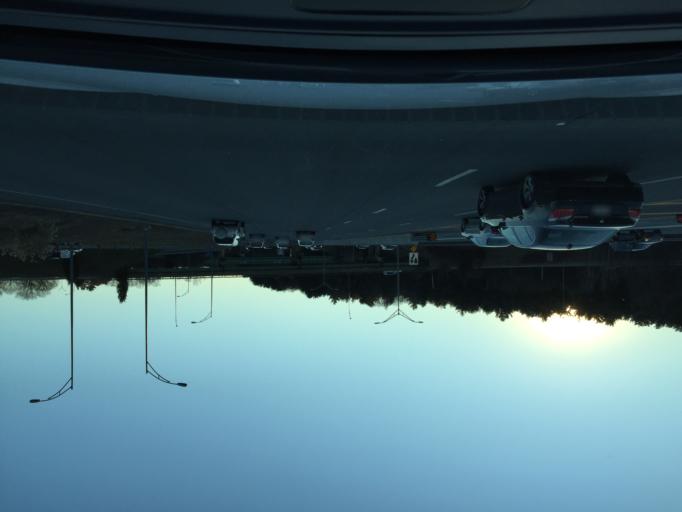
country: US
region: Massachusetts
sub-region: Middlesex County
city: Weston
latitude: 42.3392
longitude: -71.2653
